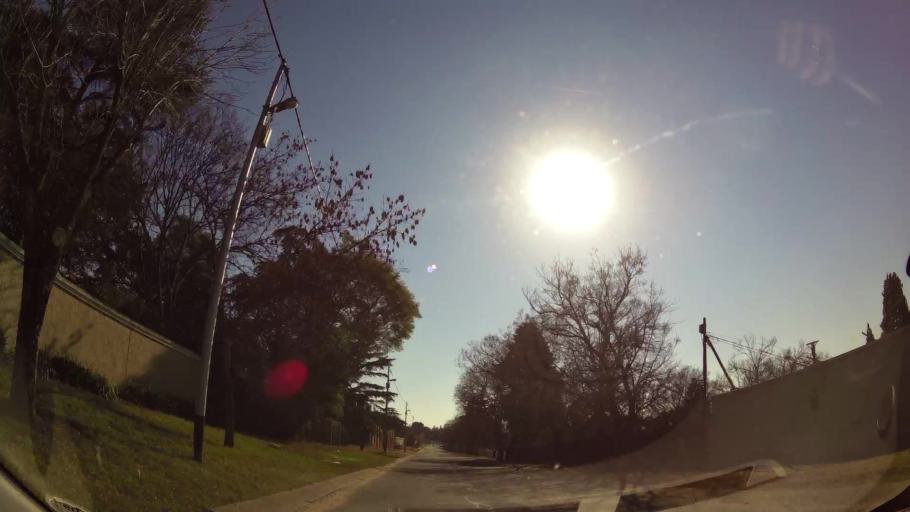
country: ZA
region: Gauteng
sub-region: City of Johannesburg Metropolitan Municipality
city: Midrand
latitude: -26.0648
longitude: 28.0393
